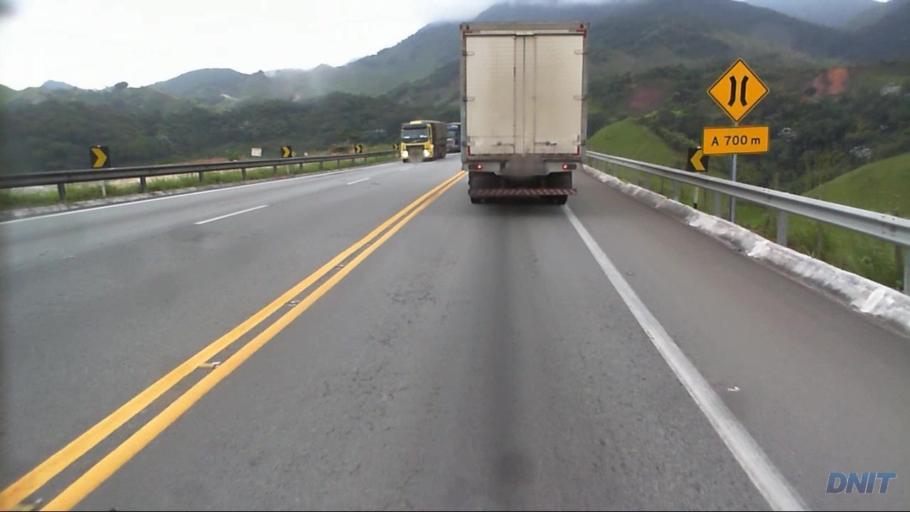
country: BR
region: Minas Gerais
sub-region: Nova Era
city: Nova Era
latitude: -19.6534
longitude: -42.9522
